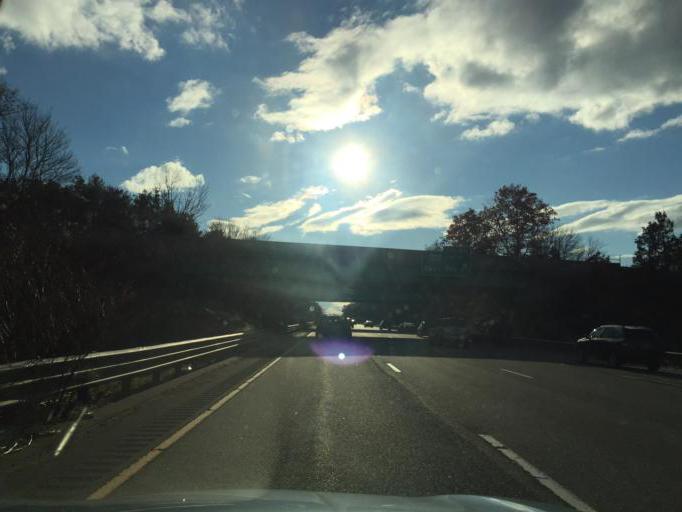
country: US
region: Massachusetts
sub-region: Bristol County
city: Mansfield
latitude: 42.0274
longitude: -71.2566
